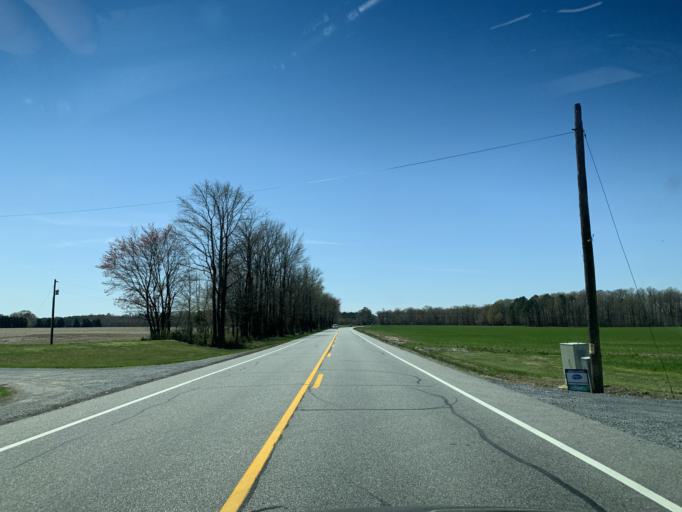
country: US
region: Maryland
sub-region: Talbot County
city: Easton
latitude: 38.8276
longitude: -76.0360
